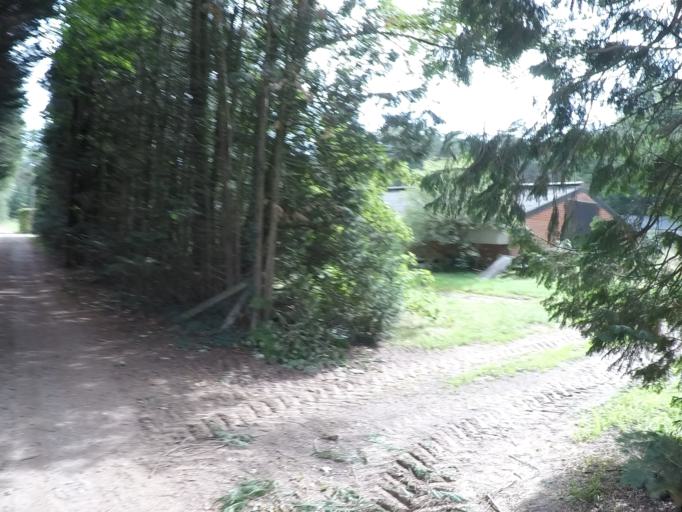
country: BE
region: Flanders
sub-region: Provincie Antwerpen
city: Vorselaar
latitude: 51.2243
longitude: 4.7712
